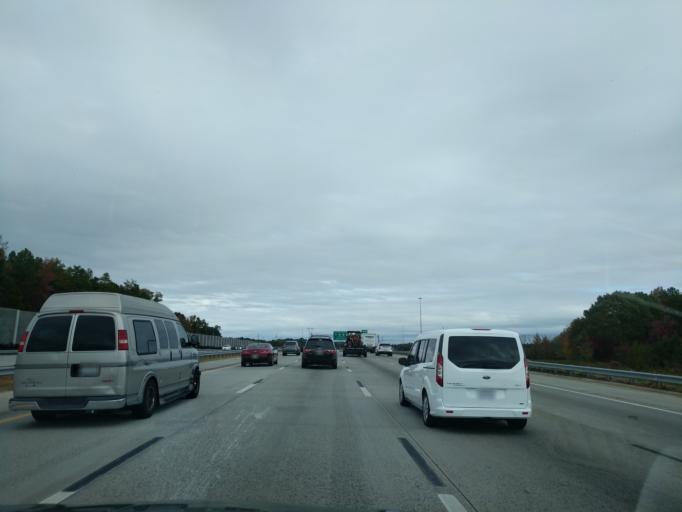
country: US
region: North Carolina
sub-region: Rowan County
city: Spencer
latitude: 35.7272
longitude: -80.3820
